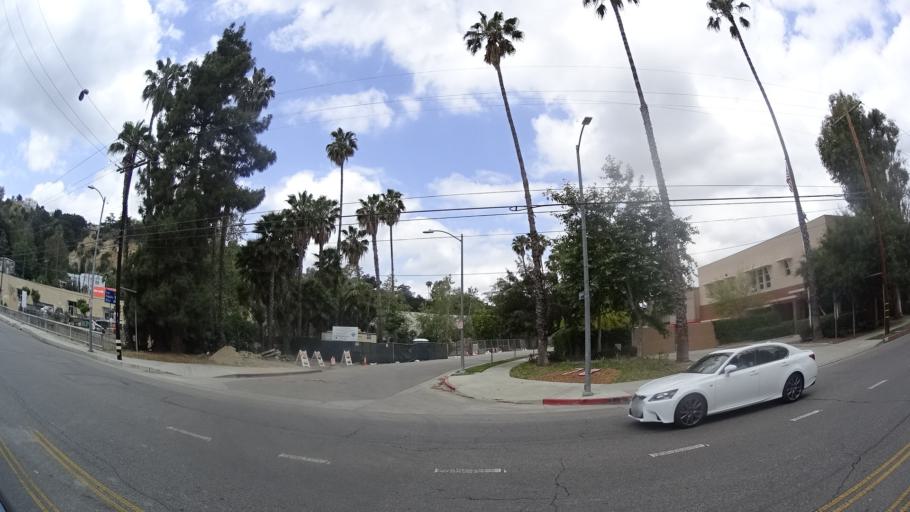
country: US
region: California
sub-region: Los Angeles County
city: North Hollywood
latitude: 34.1440
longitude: -118.4052
